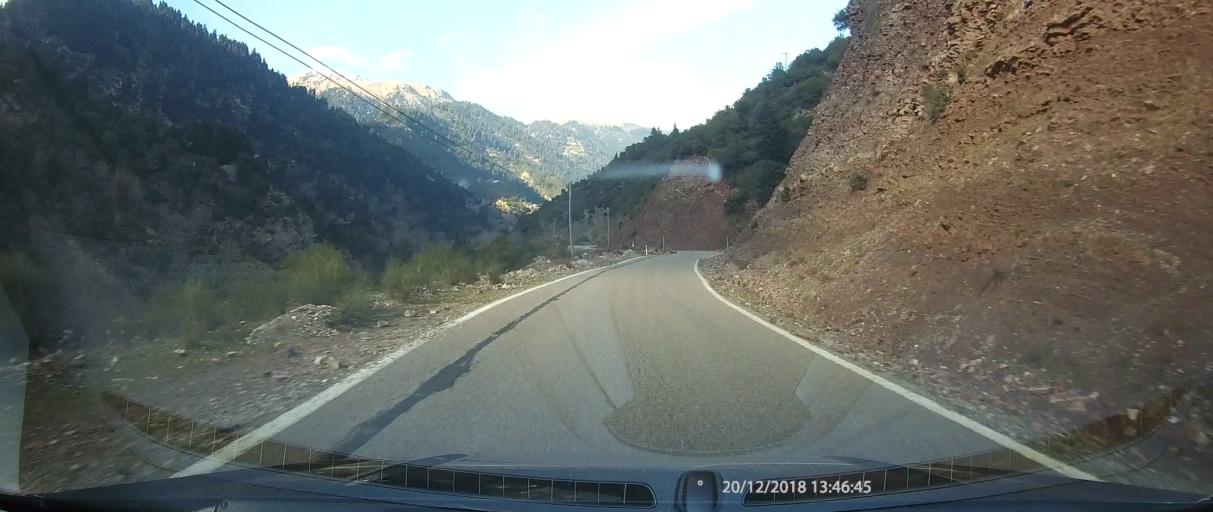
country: GR
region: West Greece
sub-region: Nomos Aitolias kai Akarnanias
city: Thermo
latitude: 38.6763
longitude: 21.6180
